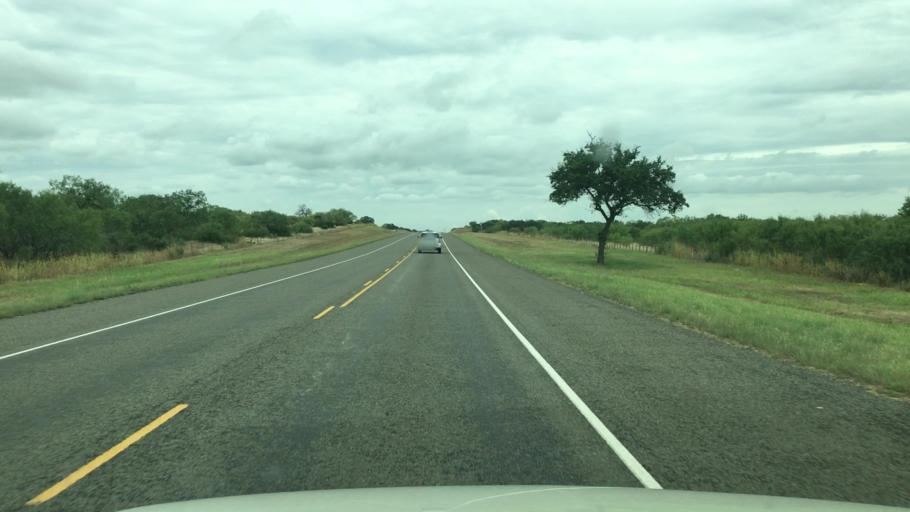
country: US
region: Texas
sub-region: Burnet County
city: Granite Shoals
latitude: 30.5615
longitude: -98.4767
